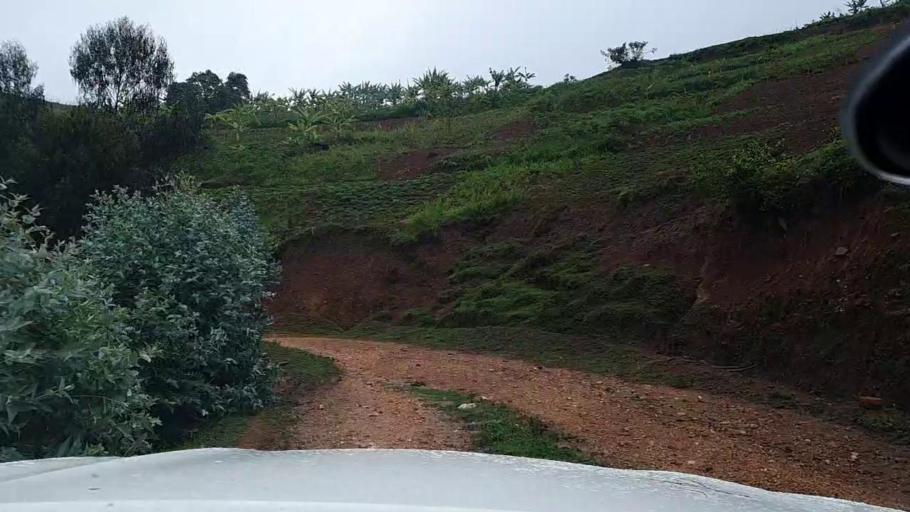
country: RW
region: Western Province
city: Kibuye
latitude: -2.1402
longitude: 29.4593
